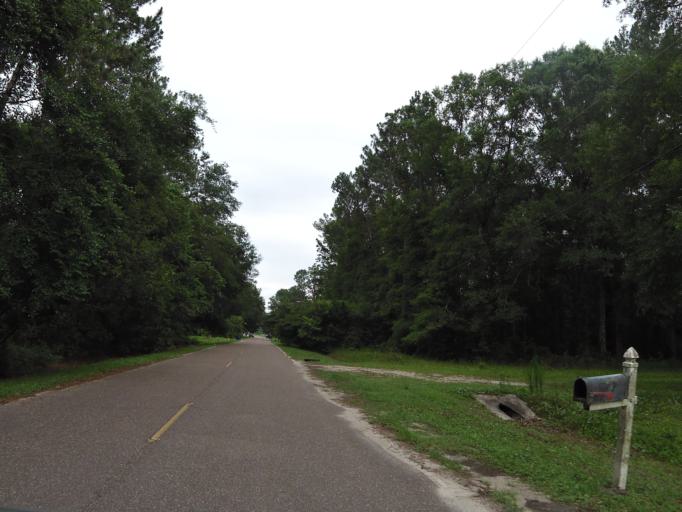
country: US
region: Florida
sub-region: Nassau County
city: Nassau Village-Ratliff
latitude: 30.5496
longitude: -81.7311
